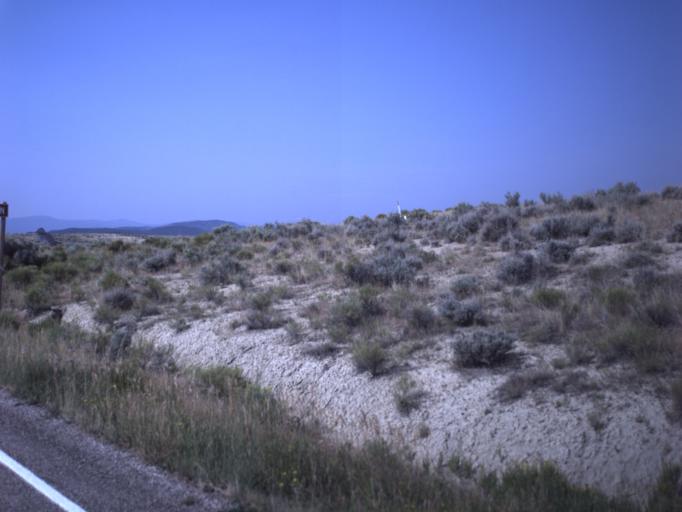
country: US
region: Utah
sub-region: Daggett County
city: Manila
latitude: 40.9951
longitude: -109.4334
